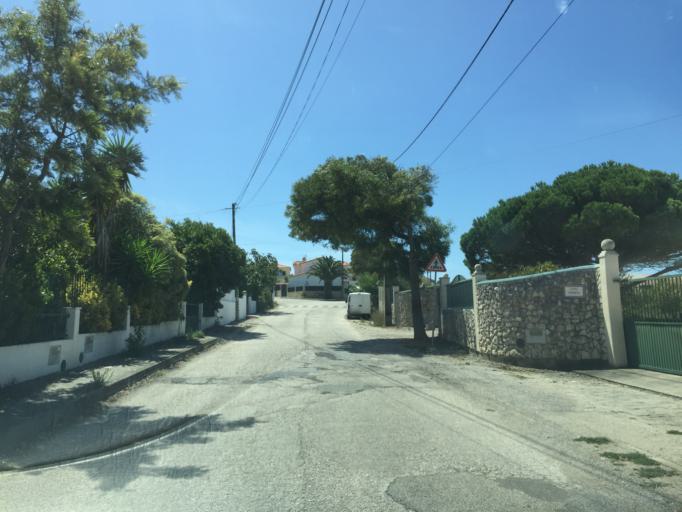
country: PT
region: Lisbon
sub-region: Lourinha
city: Lourinha
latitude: 39.2147
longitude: -9.3217
